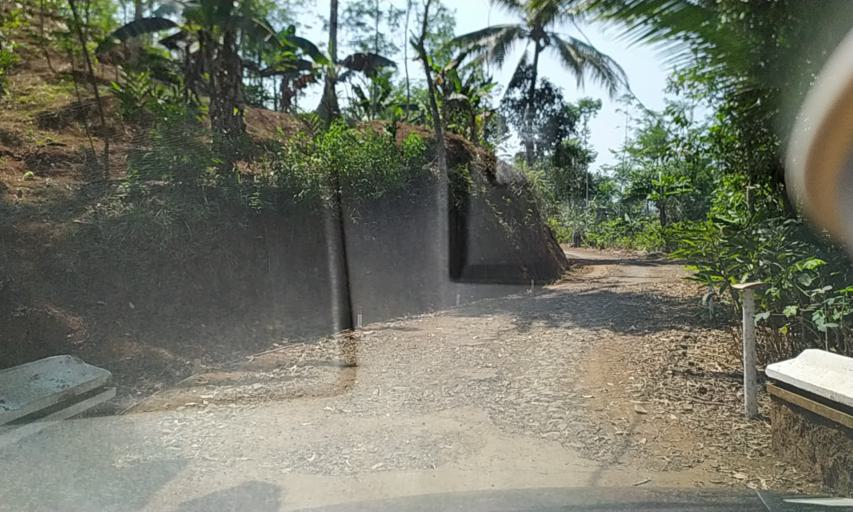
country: ID
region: Central Java
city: Kujang
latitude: -7.1930
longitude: 108.6082
